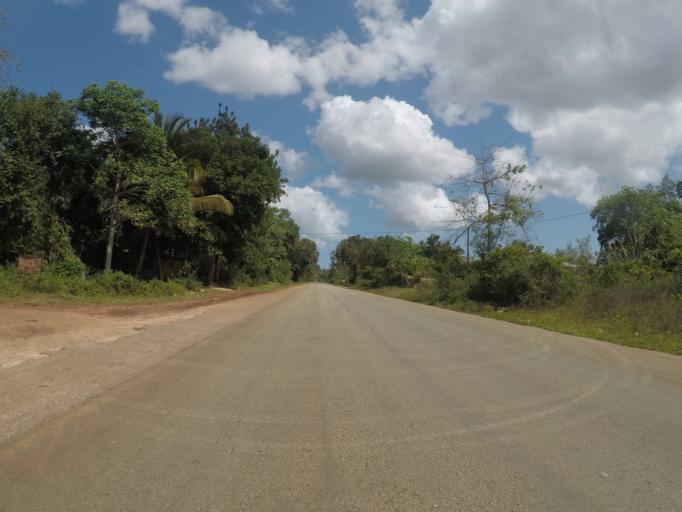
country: TZ
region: Zanzibar Central/South
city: Koani
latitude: -6.1648
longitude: 39.3301
